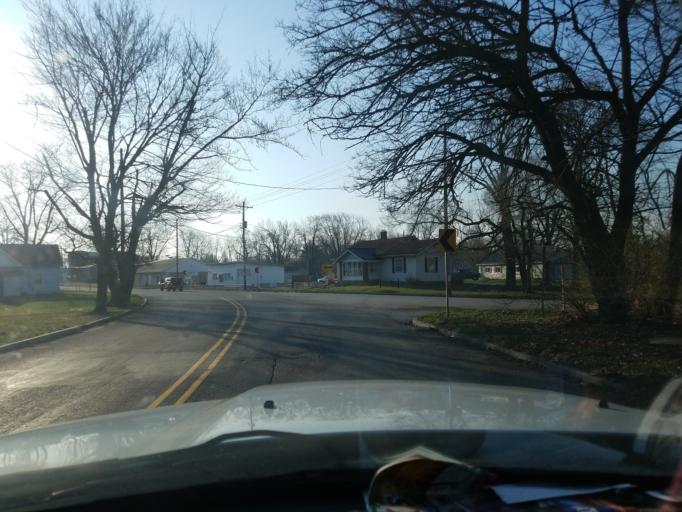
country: US
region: Indiana
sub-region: Vigo County
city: Seelyville
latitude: 39.3906
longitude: -87.3029
